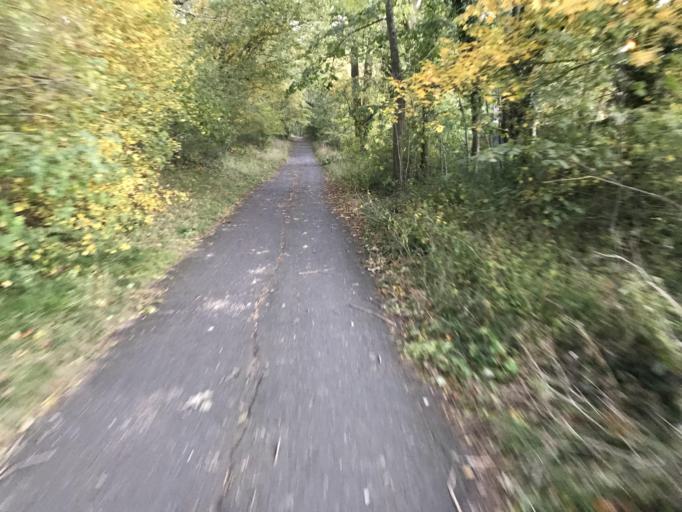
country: FR
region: Ile-de-France
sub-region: Departement de l'Essonne
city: Orsay
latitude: 48.7123
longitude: 2.1920
